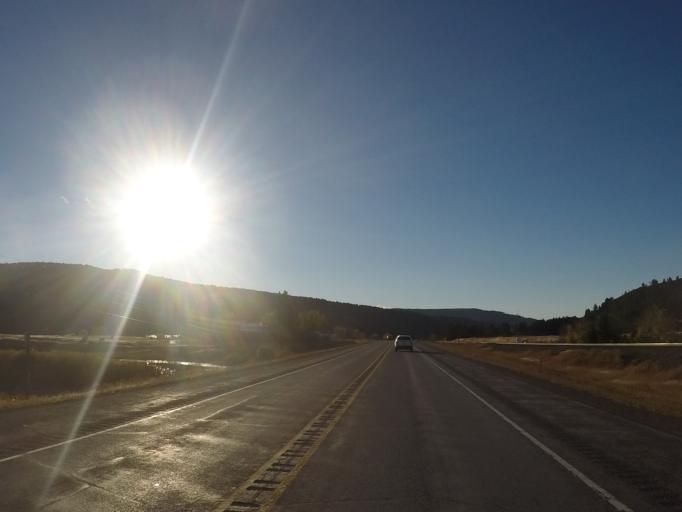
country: US
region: Montana
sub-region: Lewis and Clark County
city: Helena West Side
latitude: 46.5569
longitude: -112.3959
